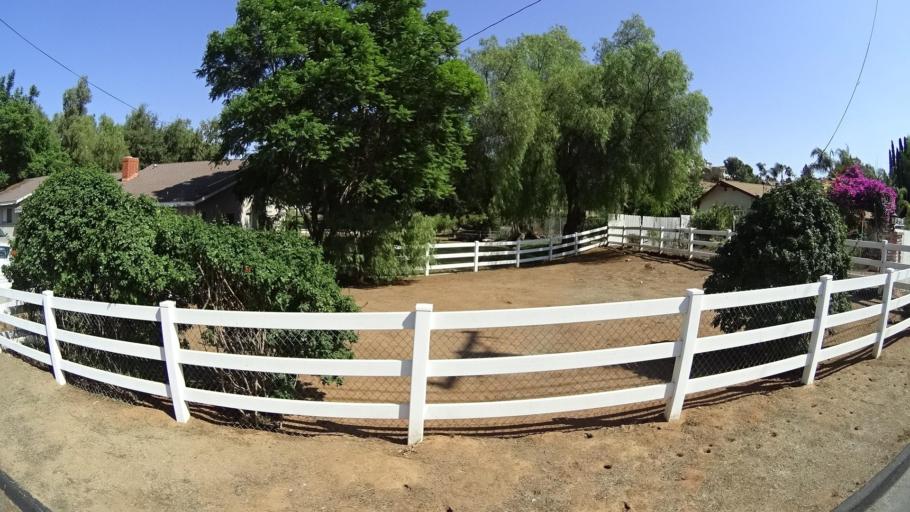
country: US
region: California
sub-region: San Diego County
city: Granite Hills
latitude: 32.7825
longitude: -116.8986
